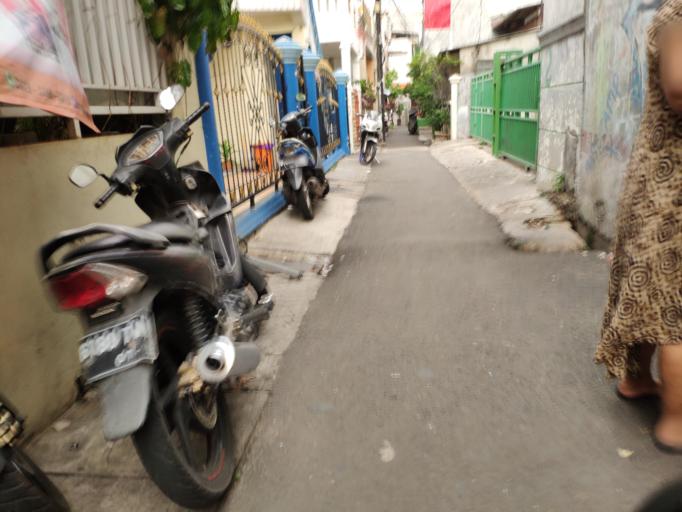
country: ID
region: Jakarta Raya
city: Jakarta
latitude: -6.1955
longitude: 106.8631
